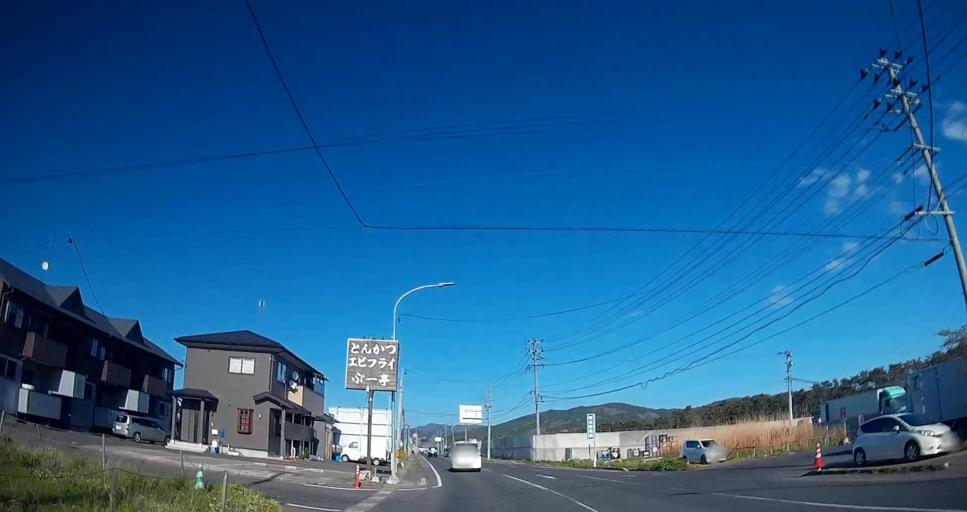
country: JP
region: Miyagi
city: Ishinomaki
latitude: 38.4172
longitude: 141.3467
